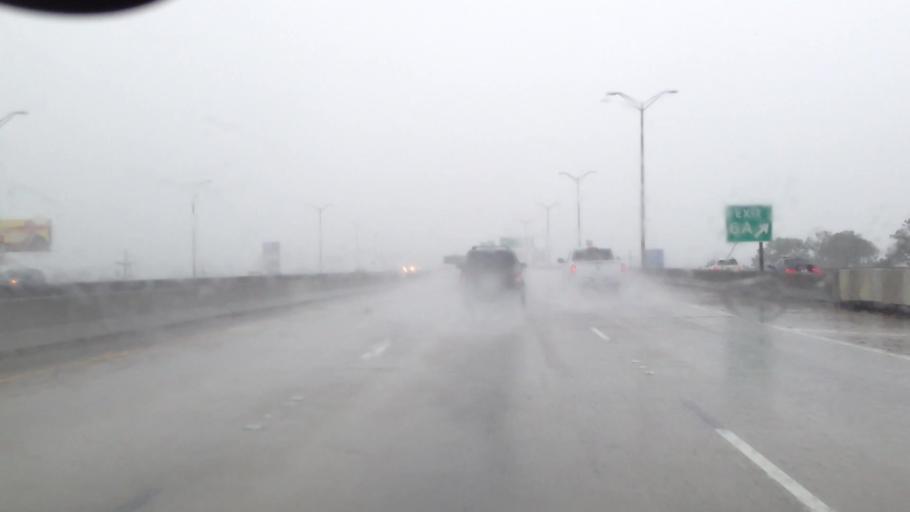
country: US
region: Louisiana
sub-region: Jefferson Parish
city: Gretna
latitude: 29.9063
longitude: -90.0626
